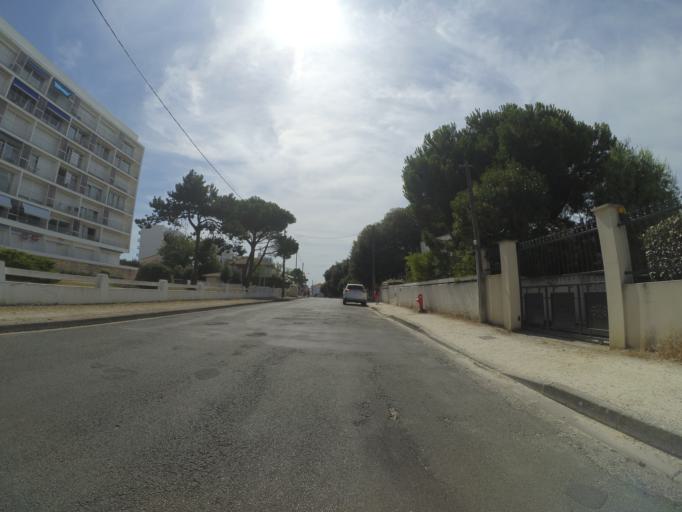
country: FR
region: Poitou-Charentes
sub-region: Departement de la Charente-Maritime
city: Saint-Georges-de-Didonne
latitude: 45.6058
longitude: -1.0089
